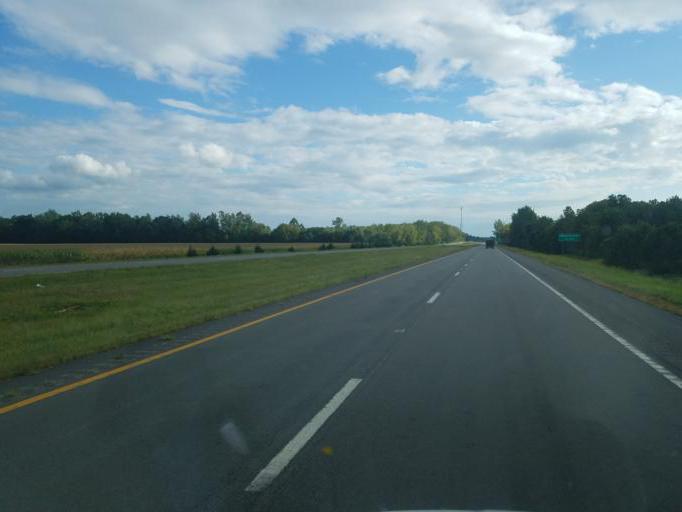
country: US
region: Ohio
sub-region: Knox County
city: Fredericktown
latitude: 40.4999
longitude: -82.5562
